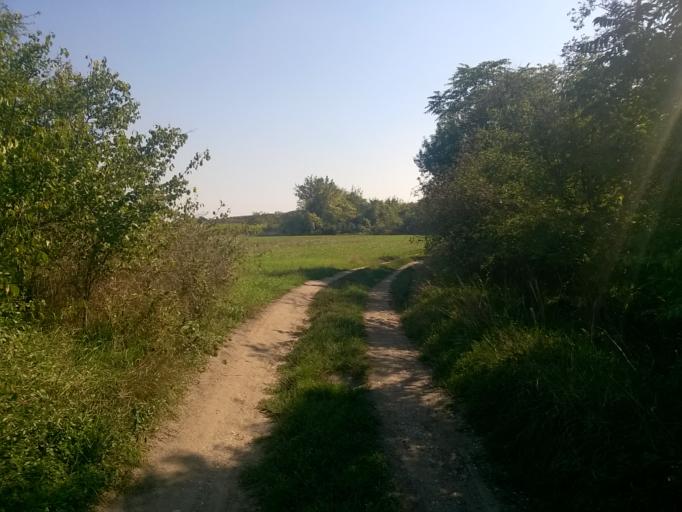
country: HU
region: Pest
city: Szazhalombatta
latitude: 47.3431
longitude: 18.9423
